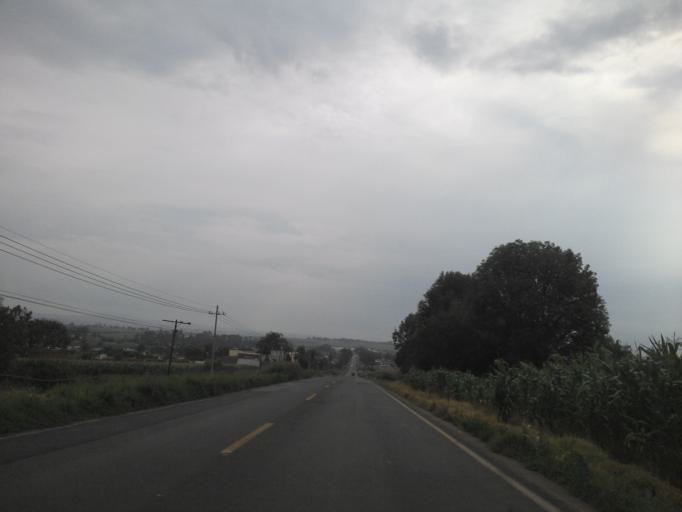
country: MX
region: Jalisco
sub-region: Acatic
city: Tierras Coloradas
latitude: 20.7397
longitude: -102.8531
